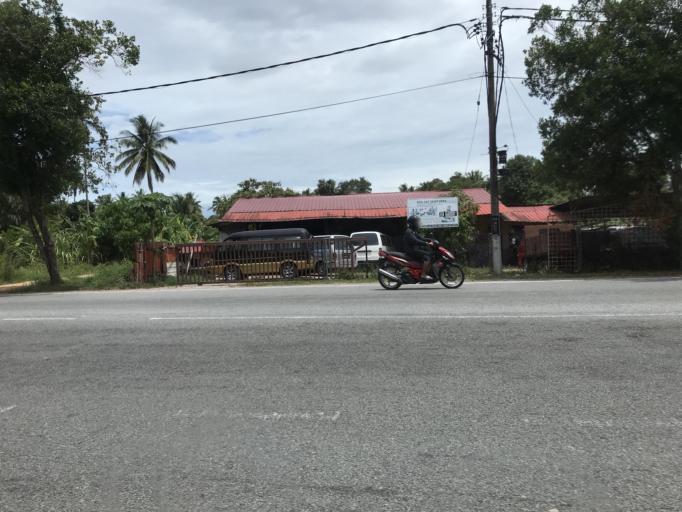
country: MY
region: Kelantan
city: Tumpat
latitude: 6.1769
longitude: 102.1801
